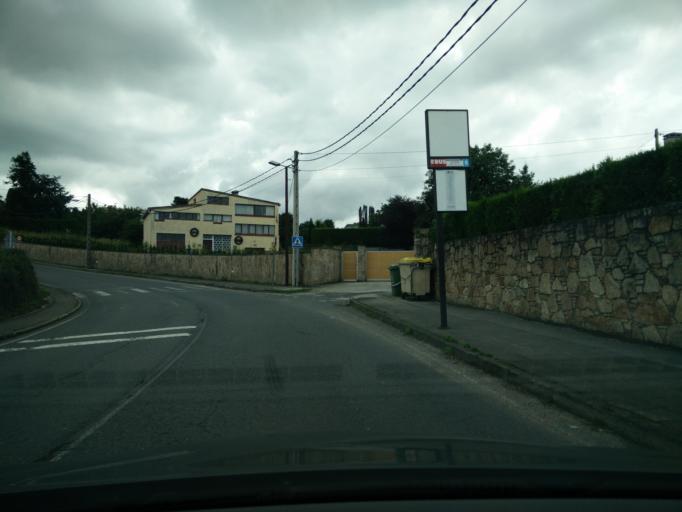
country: ES
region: Galicia
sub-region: Provincia da Coruna
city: Culleredo
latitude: 43.3280
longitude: -8.4035
